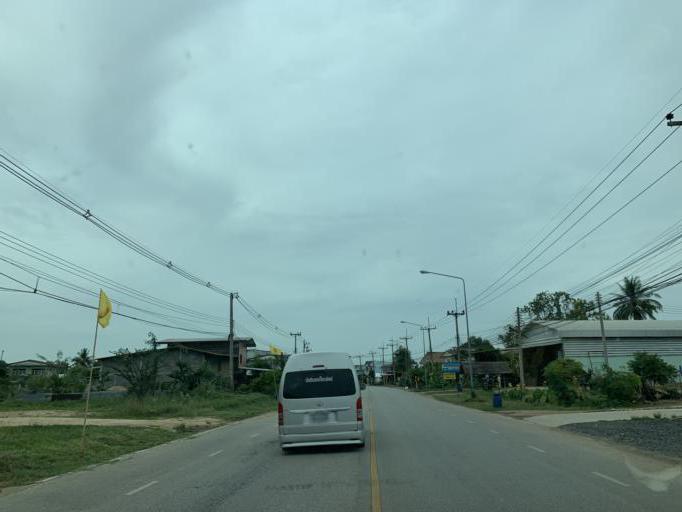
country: TH
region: Nakhon Sawan
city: Lat Yao
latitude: 15.7945
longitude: 99.6763
